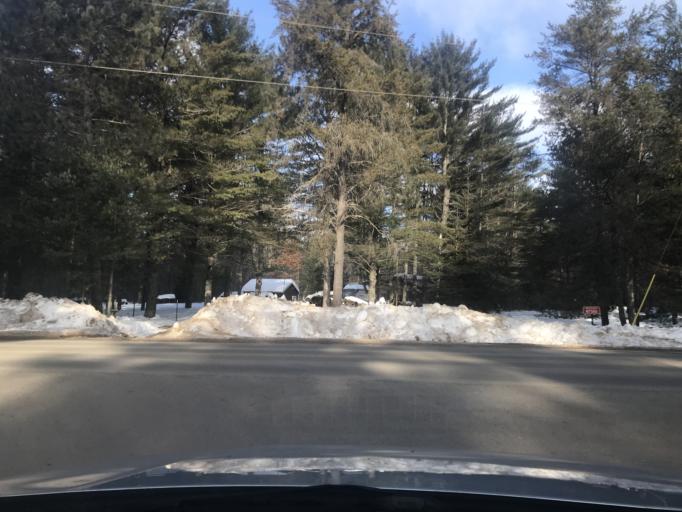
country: US
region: Wisconsin
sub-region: Marinette County
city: Niagara
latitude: 45.6376
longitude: -87.9707
